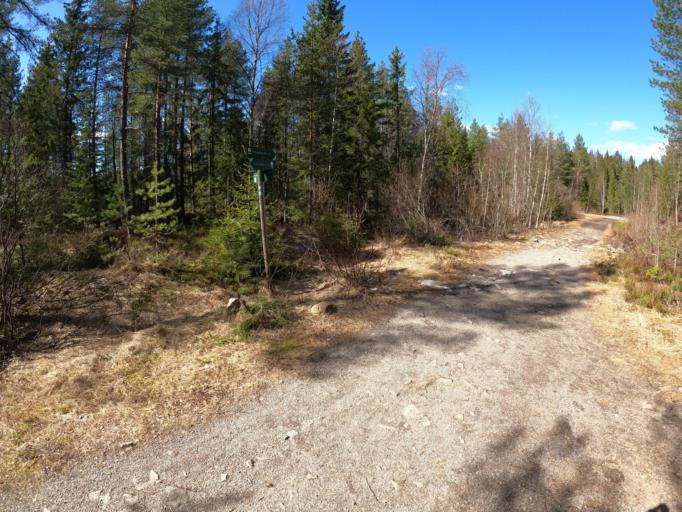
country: NO
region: Akershus
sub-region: Gjerdrum
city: Ask
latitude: 60.0444
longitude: 10.9945
